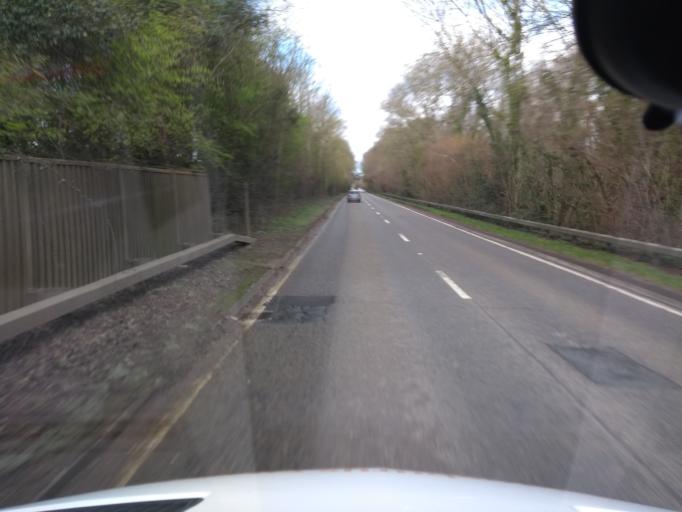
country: GB
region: England
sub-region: Somerset
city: Stoke-sub-Hamdon
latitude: 50.9473
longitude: -2.6916
